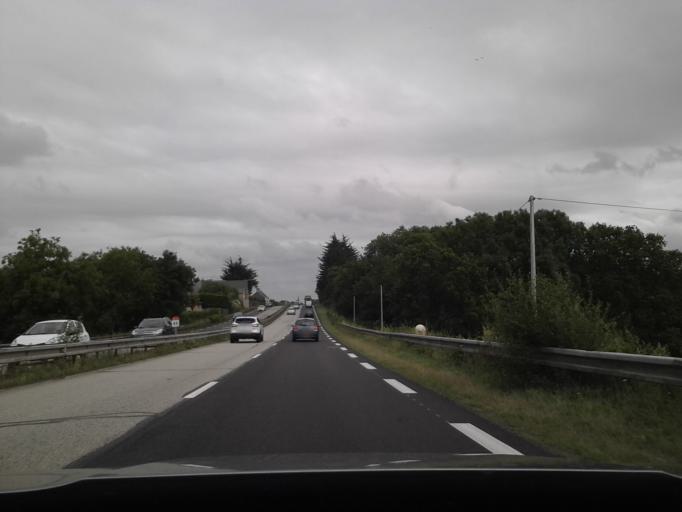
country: FR
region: Lower Normandy
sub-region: Departement de la Manche
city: Brix
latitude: 49.5441
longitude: -1.5529
